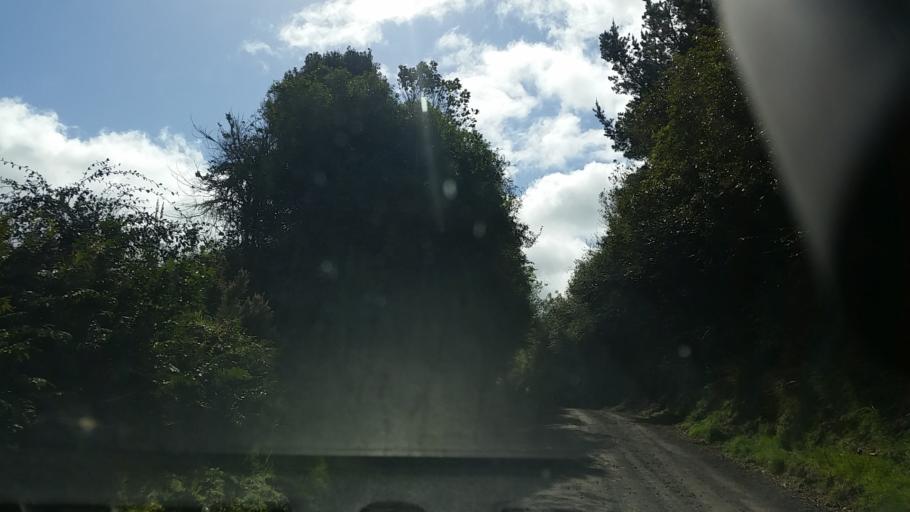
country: NZ
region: Bay of Plenty
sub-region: Rotorua District
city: Rotorua
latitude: -38.3723
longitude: 176.1222
